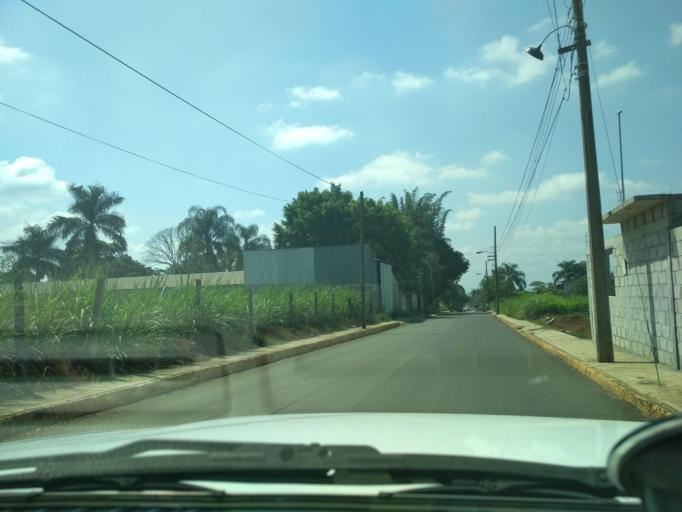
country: MX
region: Veracruz
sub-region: Fortin
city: Fraccionamiento los Alamos
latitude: 18.9165
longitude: -96.9753
